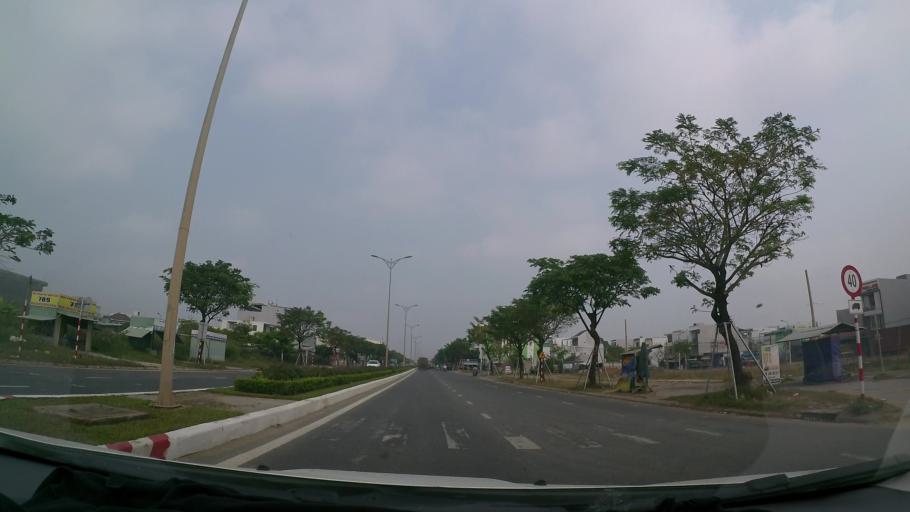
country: VN
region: Da Nang
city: Cam Le
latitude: 16.0083
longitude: 108.2192
